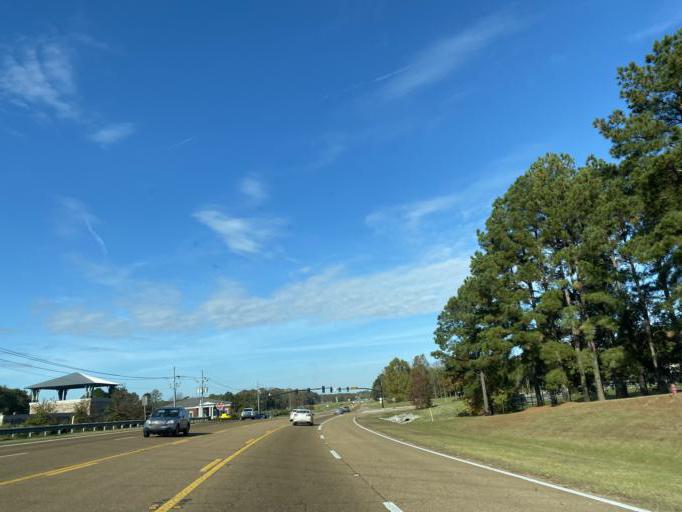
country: US
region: Mississippi
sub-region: Madison County
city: Madison
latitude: 32.4733
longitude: -90.1484
